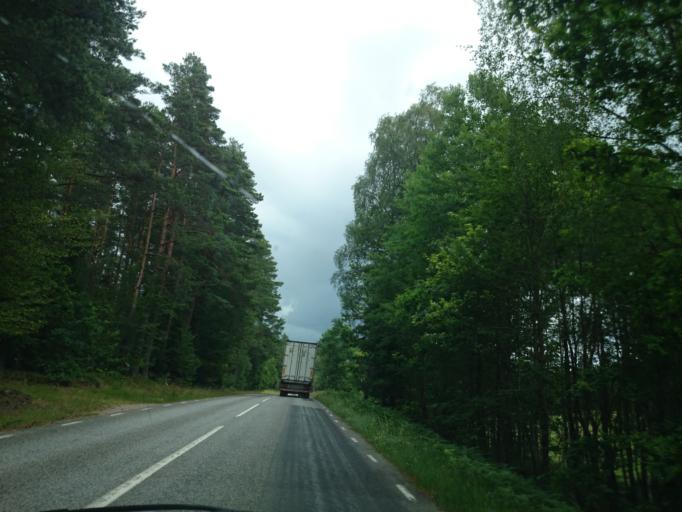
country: SE
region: Joenkoeping
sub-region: Varnamo Kommun
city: Varnamo
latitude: 57.0837
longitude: 13.9544
